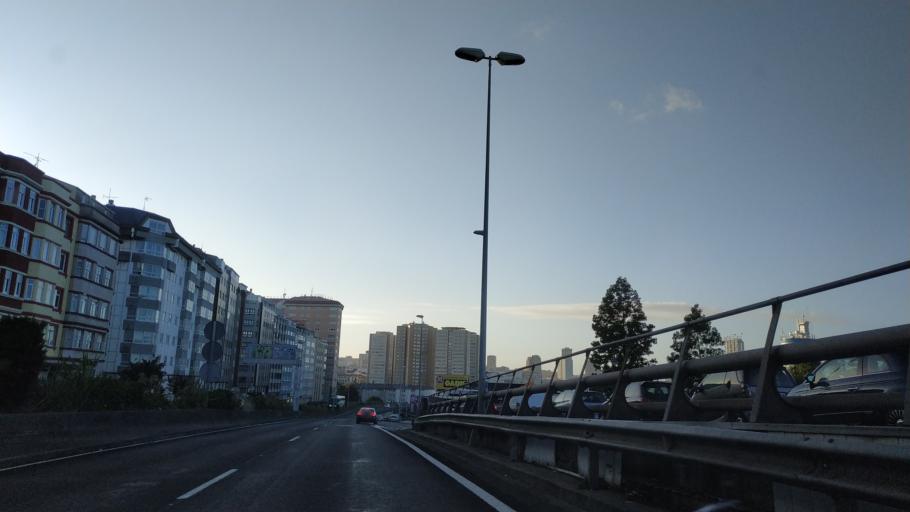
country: ES
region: Galicia
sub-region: Provincia da Coruna
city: A Coruna
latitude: 43.3539
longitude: -8.3924
